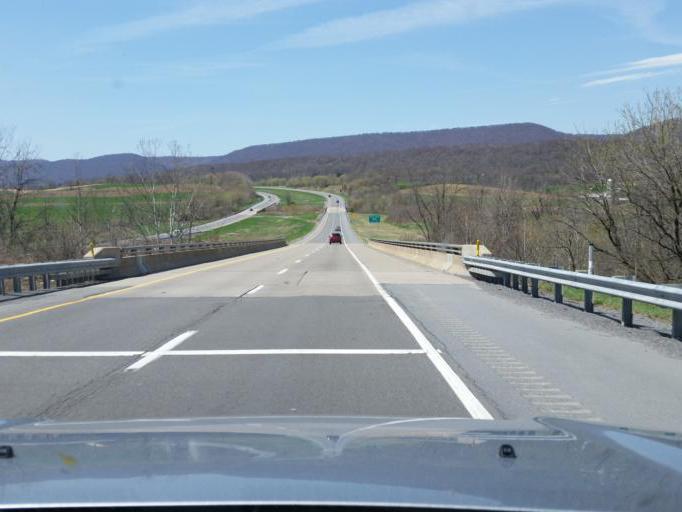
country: US
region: Pennsylvania
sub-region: Juniata County
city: Mifflintown
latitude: 40.6007
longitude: -77.3888
